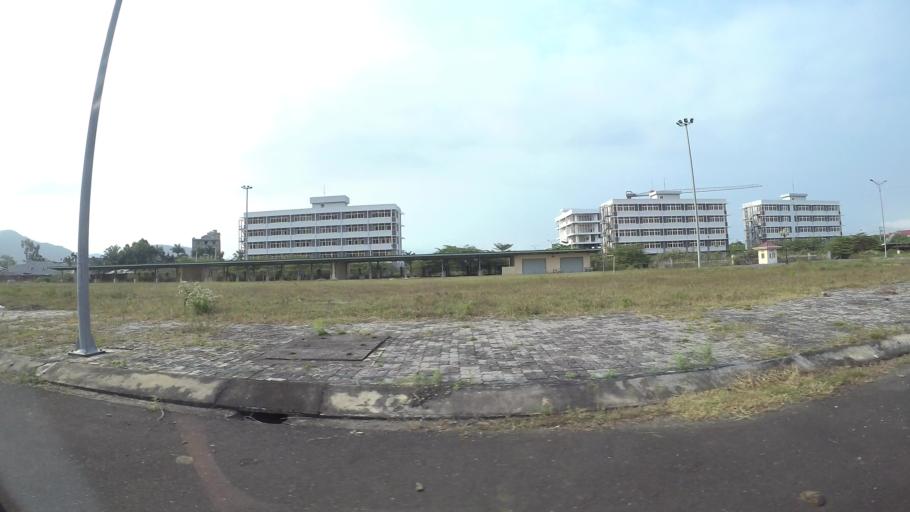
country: VN
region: Da Nang
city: Lien Chieu
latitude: 16.0477
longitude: 108.1594
